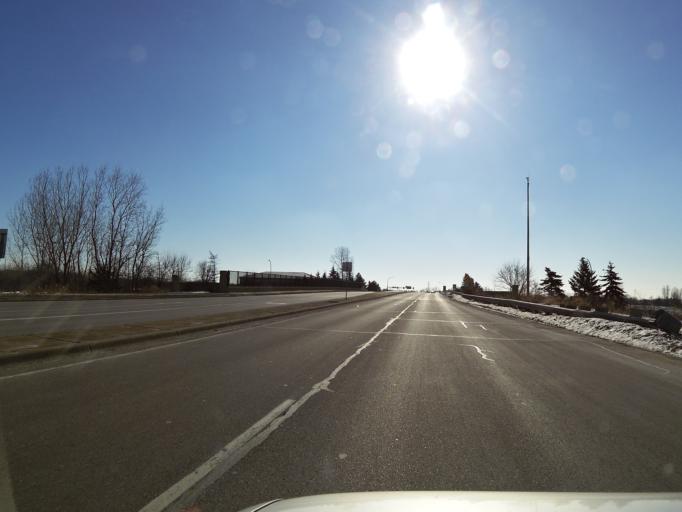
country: US
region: Minnesota
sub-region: Washington County
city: Woodbury
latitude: 44.9168
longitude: -92.9806
